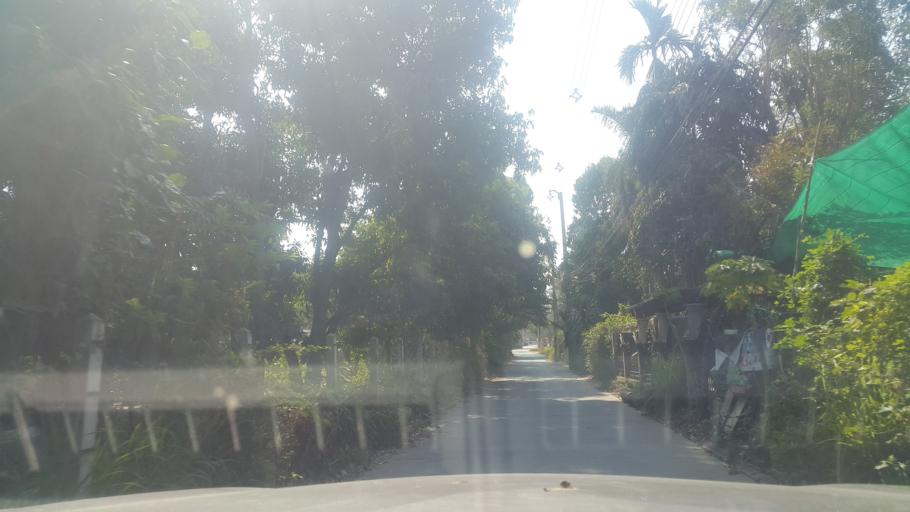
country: TH
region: Nakhon Ratchasima
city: Nakhon Ratchasima
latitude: 14.9328
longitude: 102.0517
